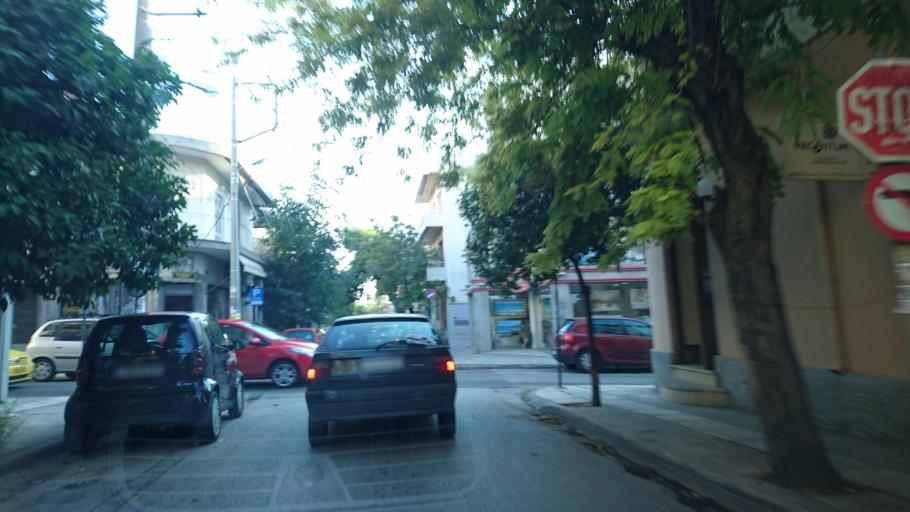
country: GR
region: Attica
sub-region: Nomarchia Athinas
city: Khalandrion
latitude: 38.0214
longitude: 23.8029
